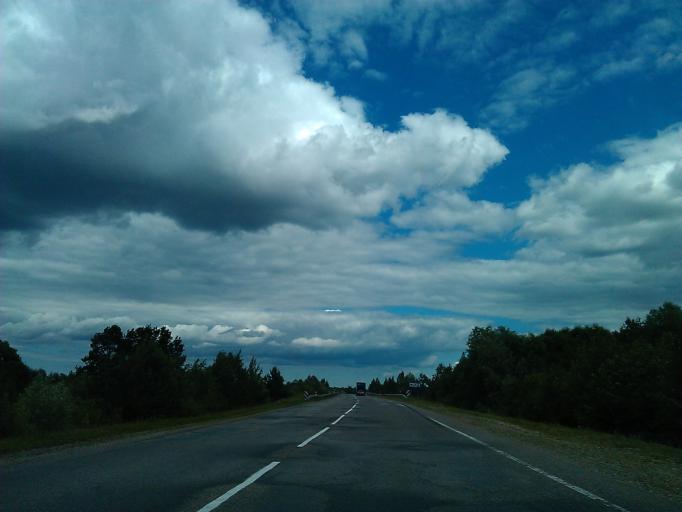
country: LV
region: Ozolnieku
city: Ozolnieki
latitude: 56.6364
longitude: 23.7712
